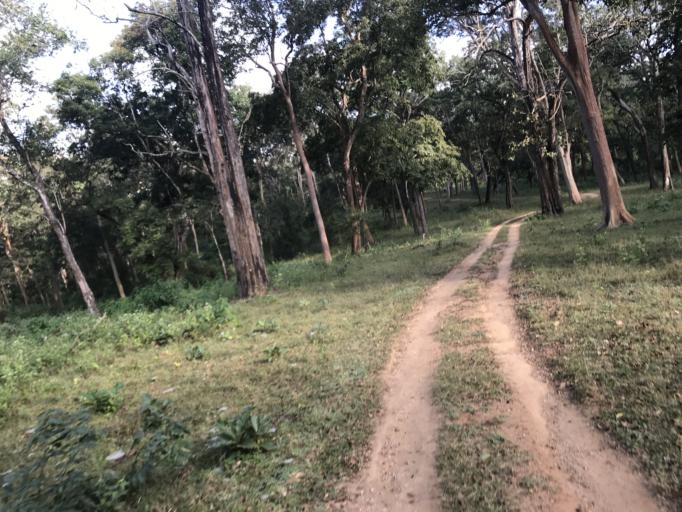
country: IN
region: Karnataka
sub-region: Mysore
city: Heggadadevankote
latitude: 11.9487
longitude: 76.1938
